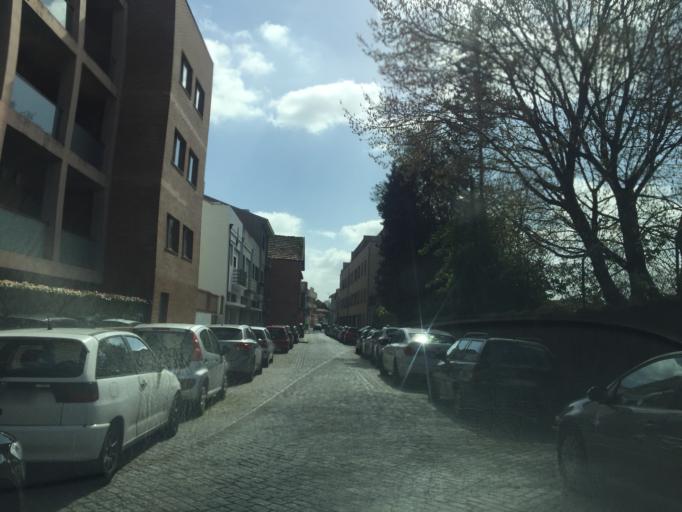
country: PT
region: Porto
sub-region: Matosinhos
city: Senhora da Hora
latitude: 41.1753
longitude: -8.6563
